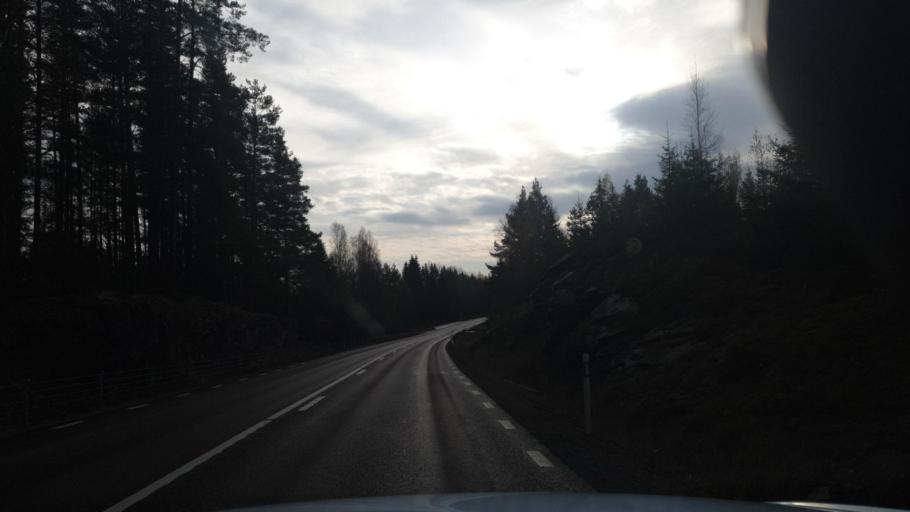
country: SE
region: Vaermland
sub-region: Karlstads Kommun
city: Edsvalla
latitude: 59.6151
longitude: 12.9820
